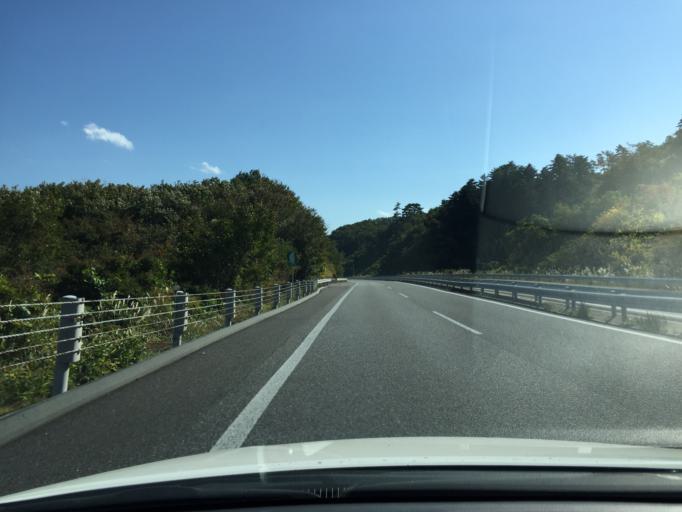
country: JP
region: Fukushima
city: Iwaki
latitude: 37.1405
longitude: 140.7485
